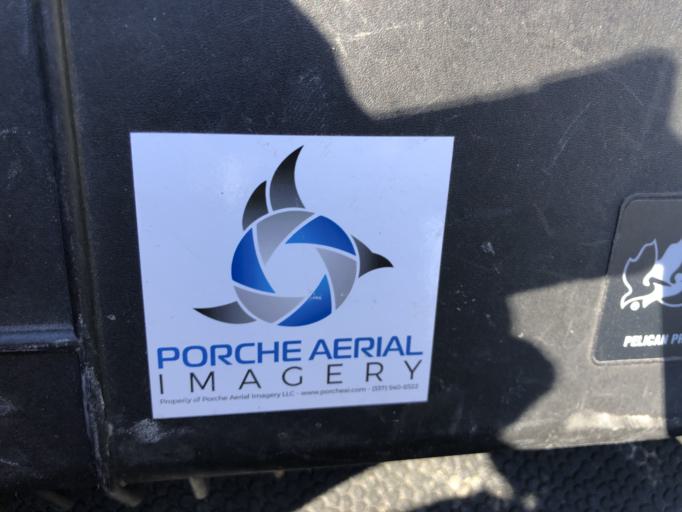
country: US
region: Louisiana
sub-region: Calcasieu Parish
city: Iowa
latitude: 30.3100
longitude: -93.0720
